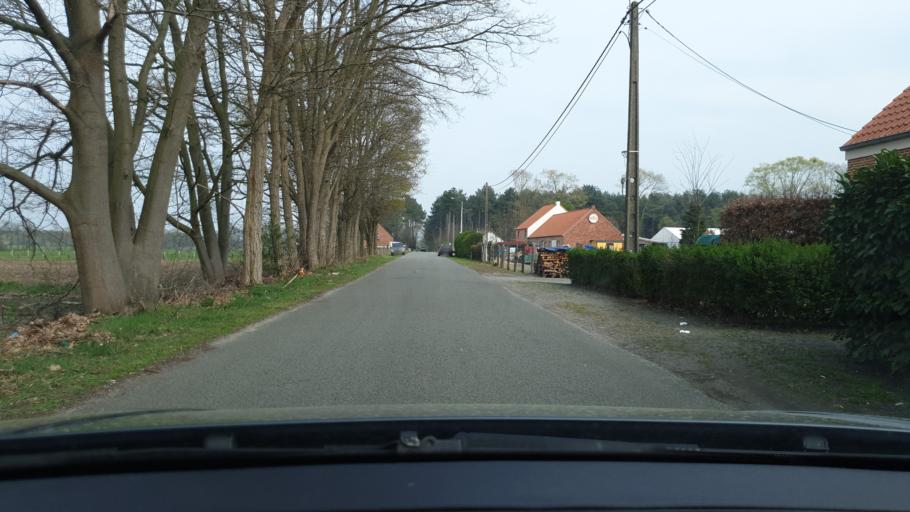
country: BE
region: Flanders
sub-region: Provincie Antwerpen
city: Laakdal
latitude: 51.1239
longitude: 5.0147
